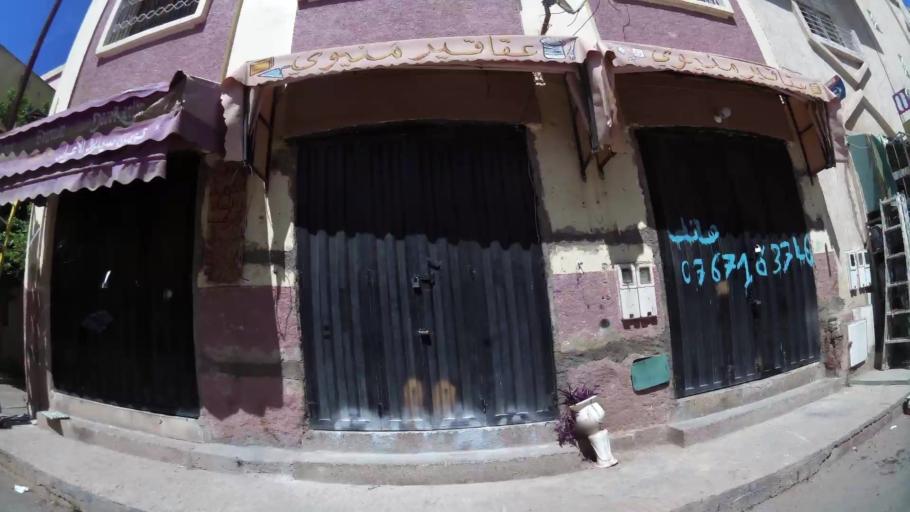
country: MA
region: Fes-Boulemane
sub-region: Fes
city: Fes
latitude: 34.0203
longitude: -5.0266
